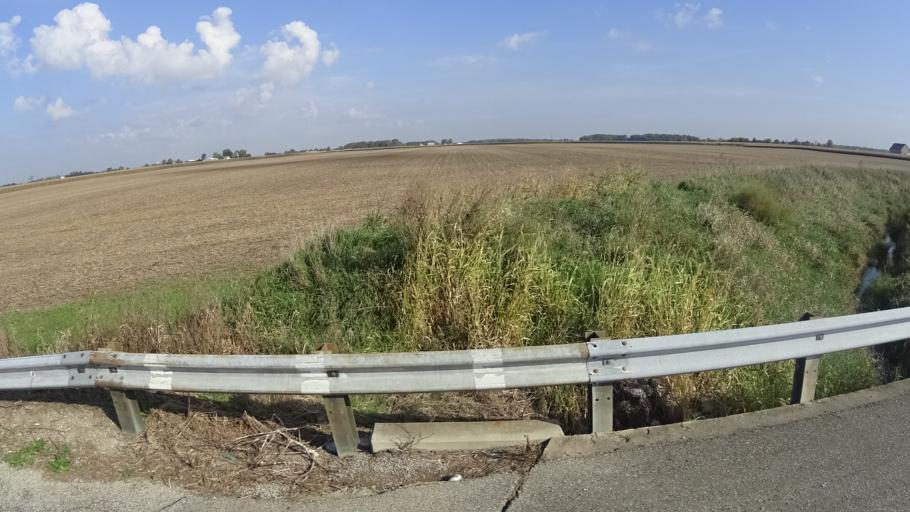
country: US
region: Indiana
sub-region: Madison County
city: Lapel
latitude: 40.0458
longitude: -85.8227
